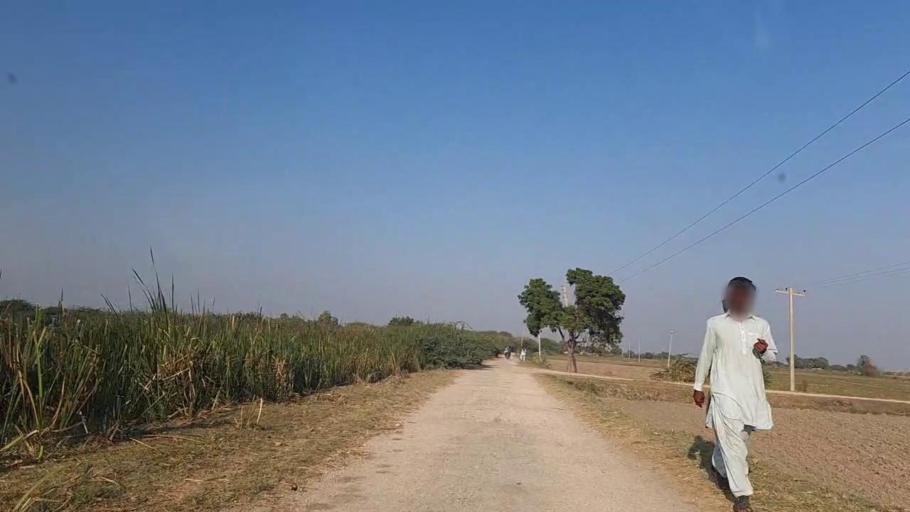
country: PK
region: Sindh
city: Thatta
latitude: 24.7185
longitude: 67.9427
